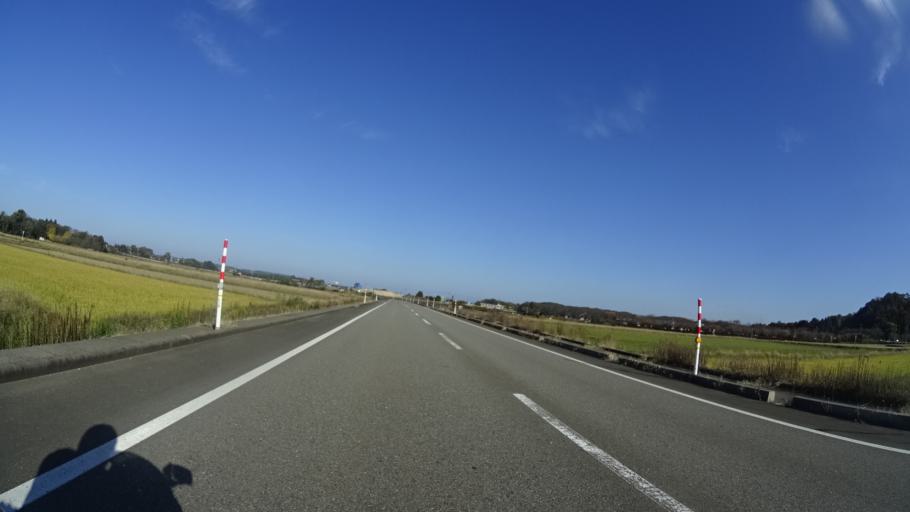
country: JP
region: Ishikawa
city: Komatsu
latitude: 36.2970
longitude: 136.3883
